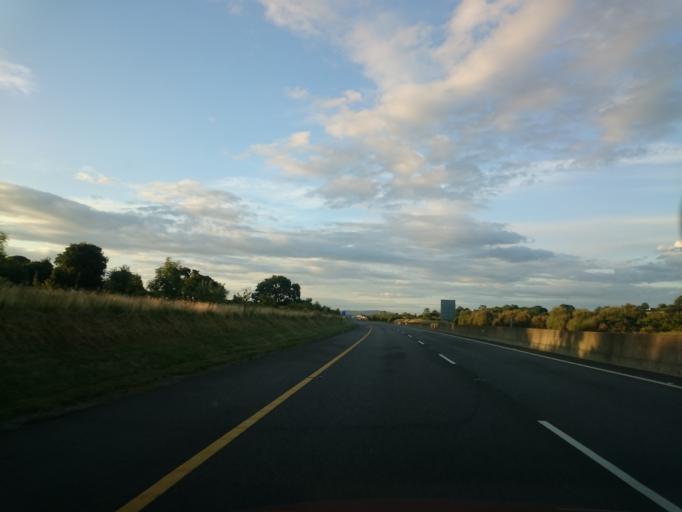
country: IE
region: Leinster
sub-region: Loch Garman
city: Castletown
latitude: 52.7174
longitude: -6.2488
